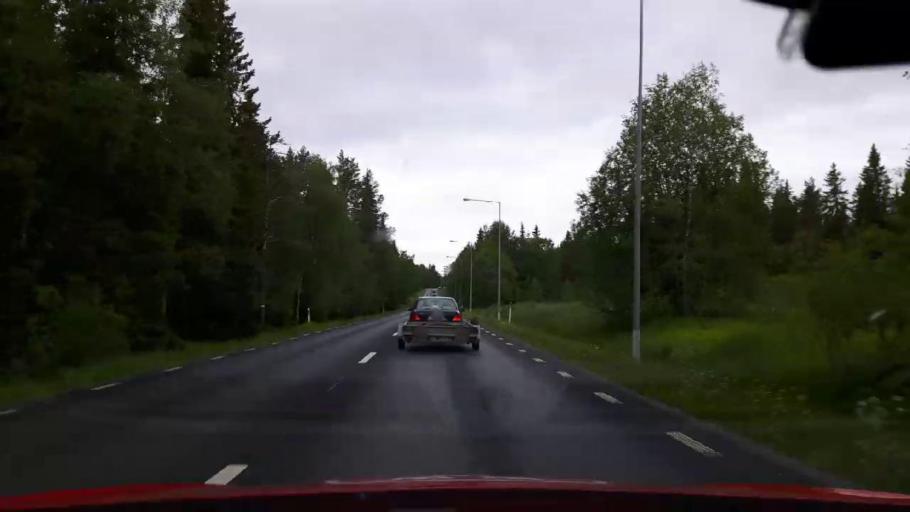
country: SE
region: Jaemtland
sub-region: OEstersunds Kommun
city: Ostersund
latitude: 63.1981
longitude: 14.6697
